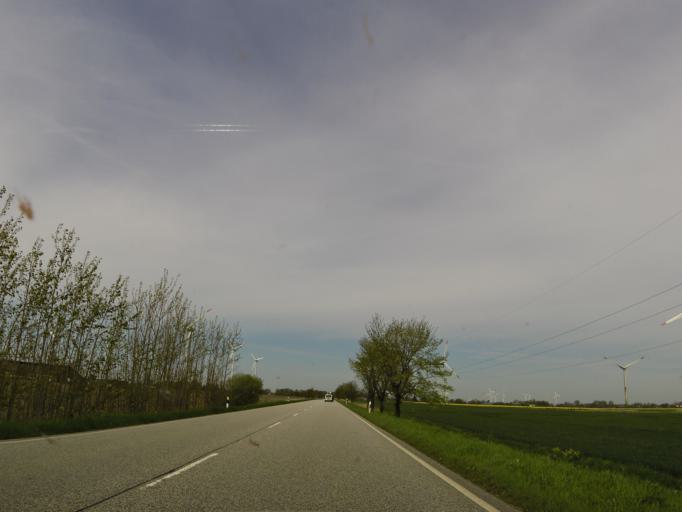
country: DE
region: Schleswig-Holstein
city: Hemme
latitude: 54.2670
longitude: 9.0248
